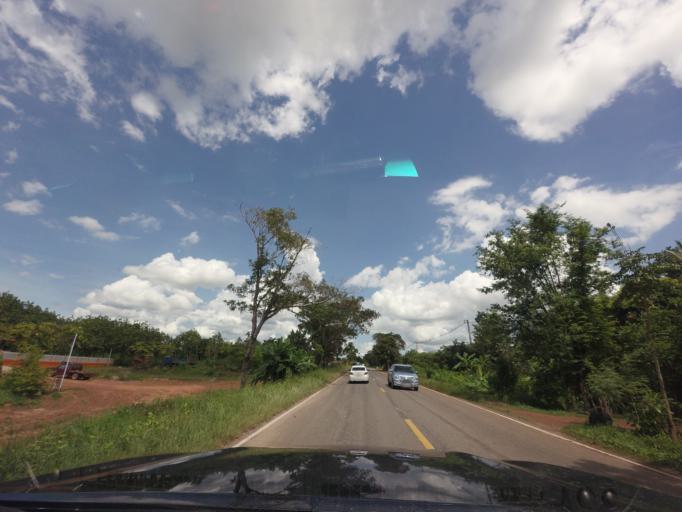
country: TH
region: Changwat Udon Thani
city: Phibun Rak
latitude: 17.6523
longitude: 103.1364
